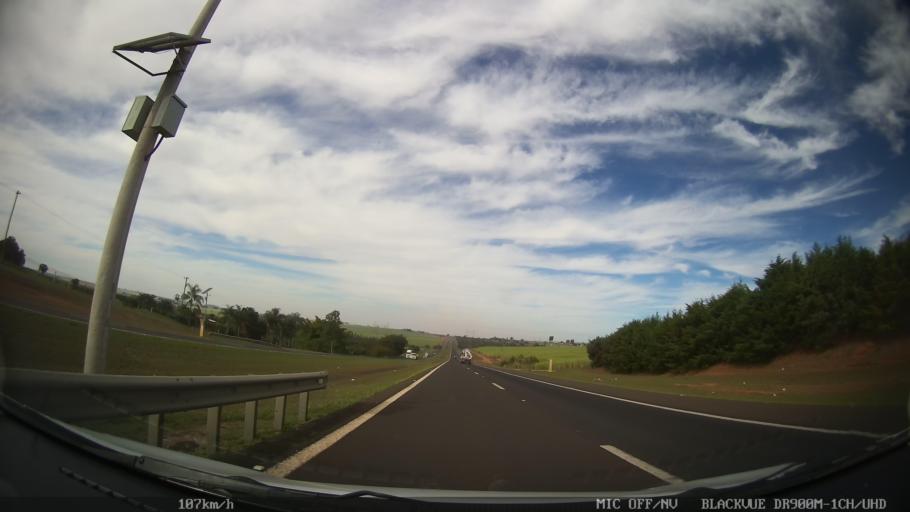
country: BR
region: Sao Paulo
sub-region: Taquaritinga
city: Taquaritinga
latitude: -21.5460
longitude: -48.4966
